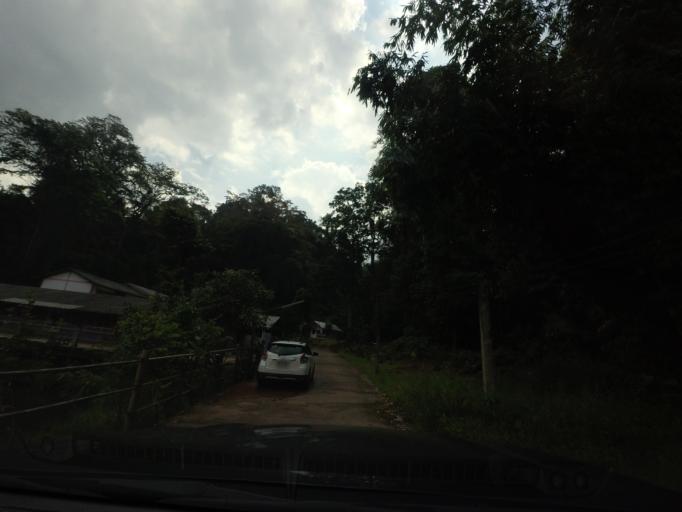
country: TH
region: Nan
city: Bo Kluea
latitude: 19.1913
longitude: 101.1991
